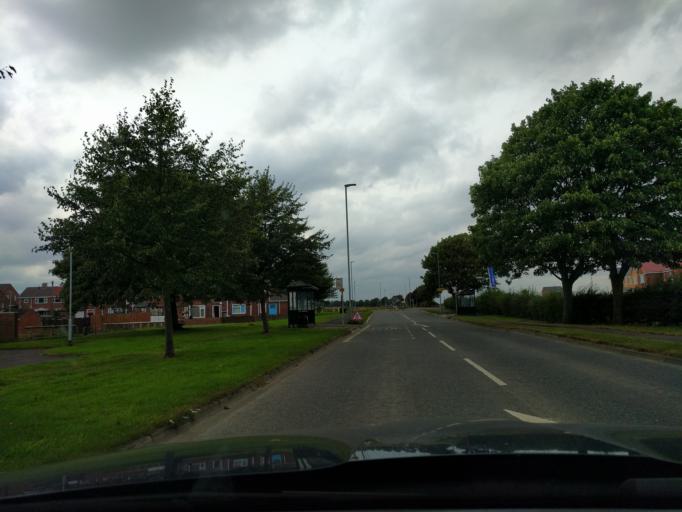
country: GB
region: England
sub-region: Northumberland
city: Choppington
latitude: 55.1332
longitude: -1.6160
